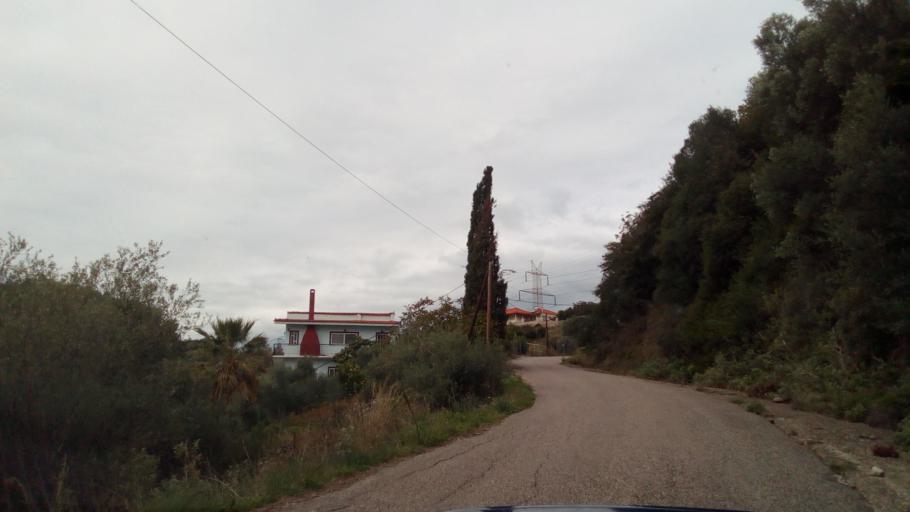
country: GR
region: West Greece
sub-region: Nomos Achaias
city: Kamarai
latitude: 38.4090
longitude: 21.9500
